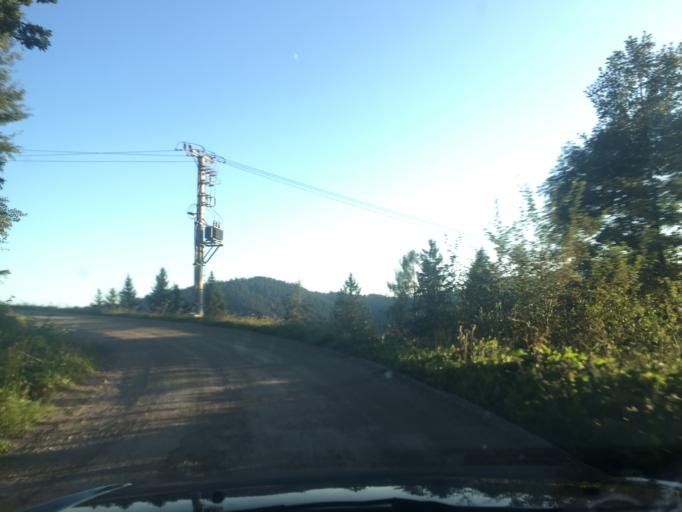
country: SI
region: Sostanj
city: Topolsica
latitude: 46.4528
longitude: 14.9936
